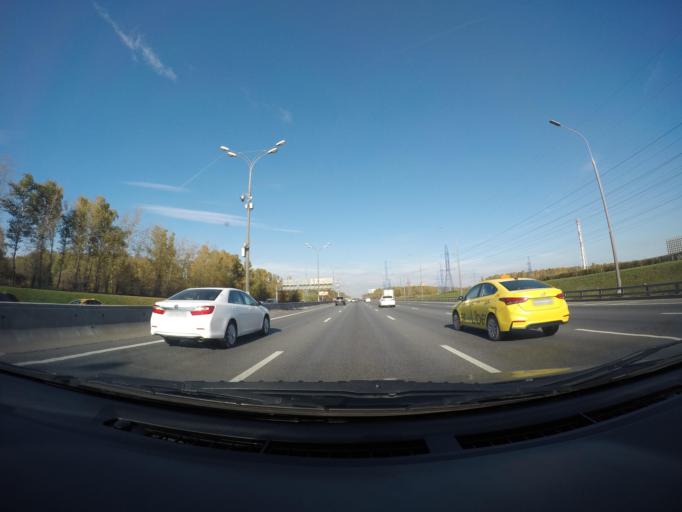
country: RU
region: Moscow
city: Ivanovskoye
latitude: 55.7844
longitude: 37.8420
